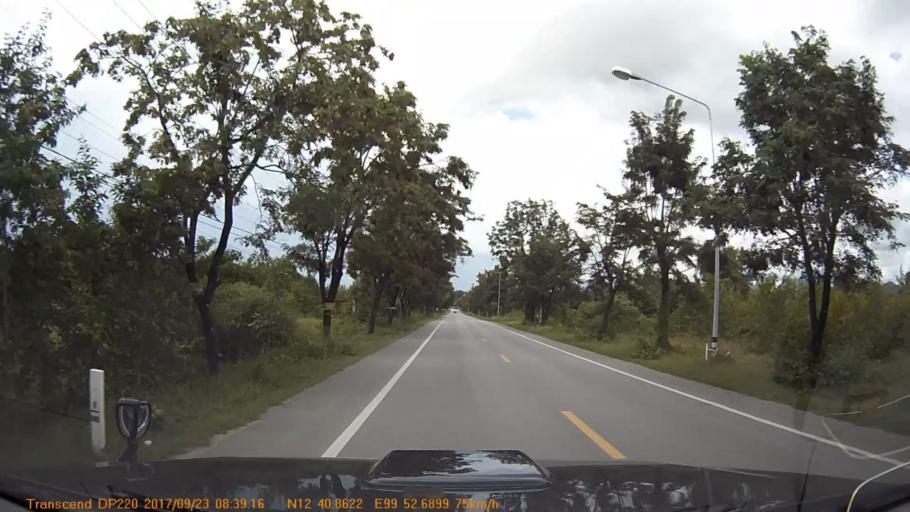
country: TH
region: Prachuap Khiri Khan
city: Hua Hin
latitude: 12.6810
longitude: 99.8782
